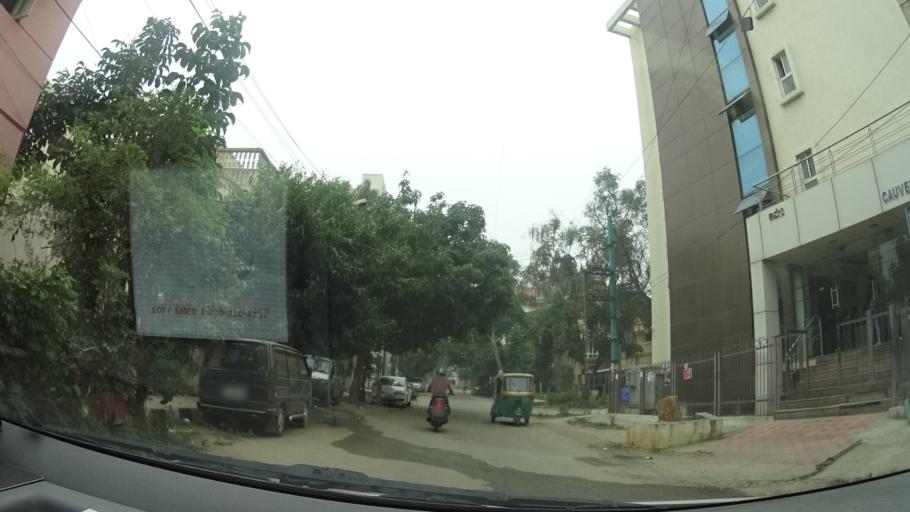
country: IN
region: Karnataka
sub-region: Bangalore Urban
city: Bangalore
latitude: 13.0313
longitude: 77.6329
